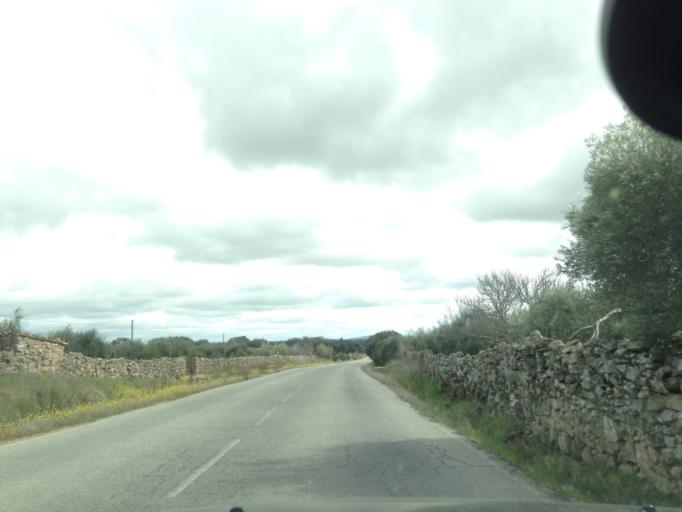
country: ES
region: Extremadura
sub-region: Provincia de Caceres
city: Albala
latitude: 39.2592
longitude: -6.1724
